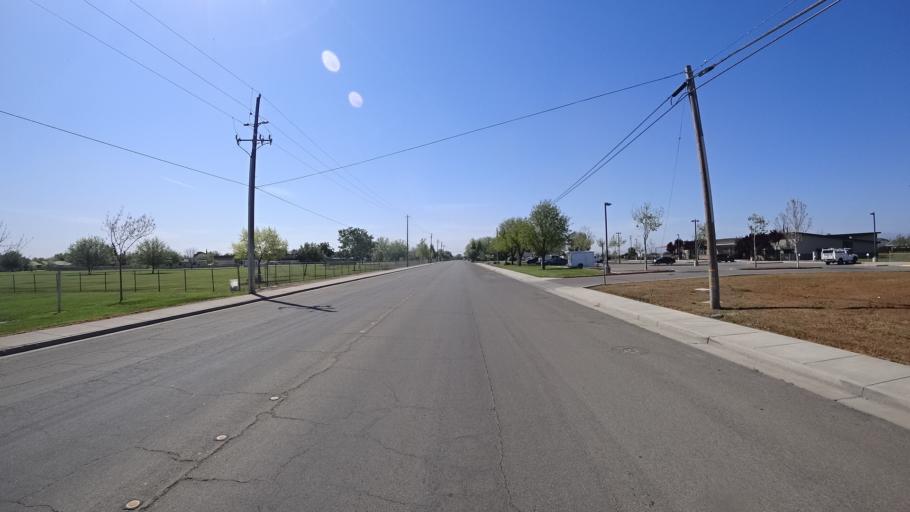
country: US
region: California
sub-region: Glenn County
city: Willows
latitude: 39.5168
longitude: -122.2088
